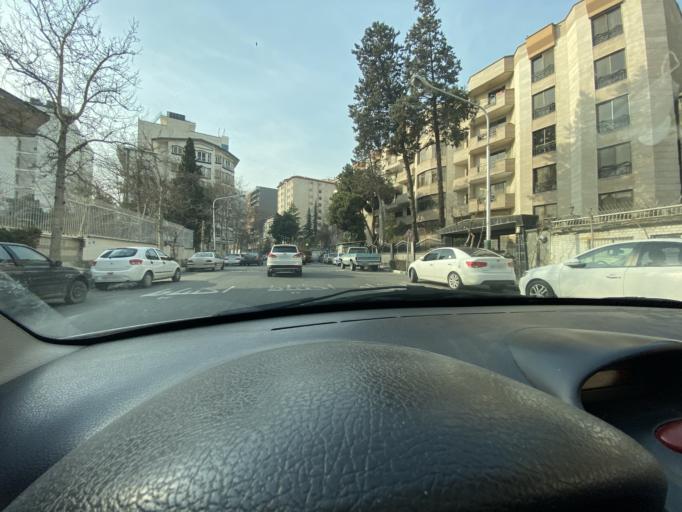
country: IR
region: Tehran
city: Tajrish
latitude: 35.8054
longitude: 51.4747
